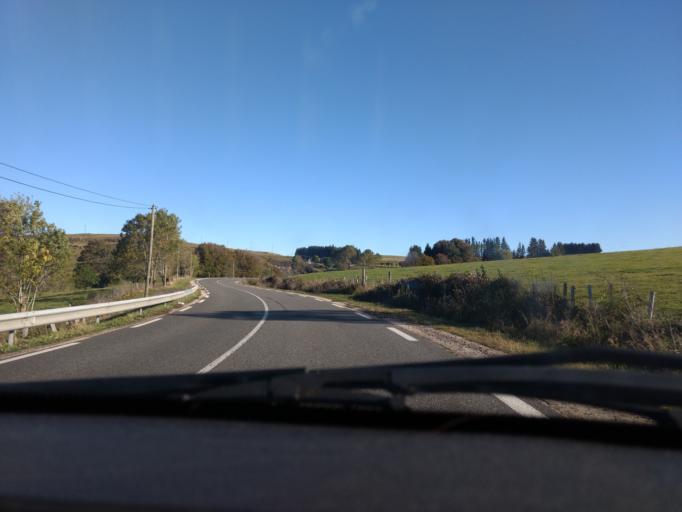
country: FR
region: Midi-Pyrenees
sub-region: Departement de l'Aveyron
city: Laguiole
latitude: 44.7178
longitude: 2.8669
